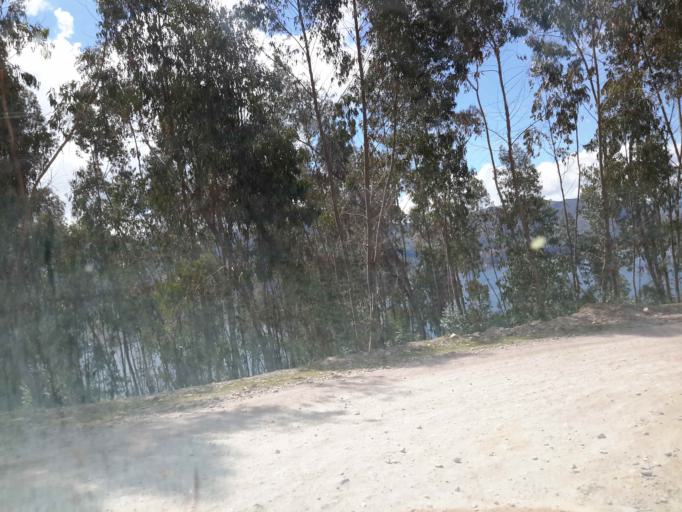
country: PE
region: Apurimac
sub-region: Provincia de Andahuaylas
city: Pacucha
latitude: -13.6193
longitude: -73.3365
